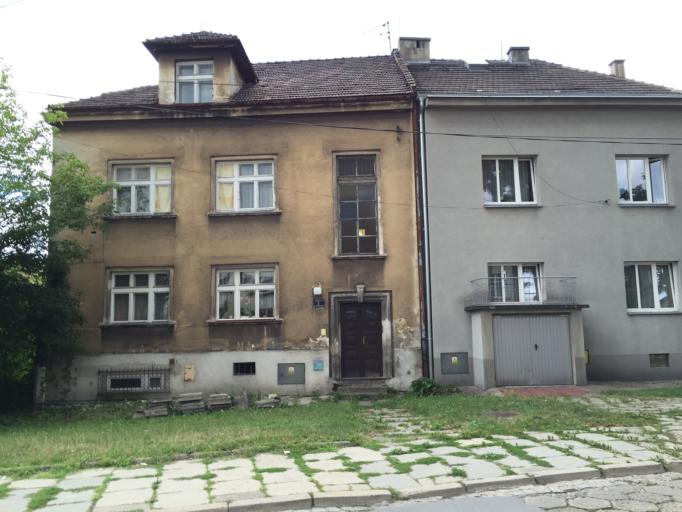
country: PL
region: Lesser Poland Voivodeship
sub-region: Krakow
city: Krakow
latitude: 50.0418
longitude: 19.9545
